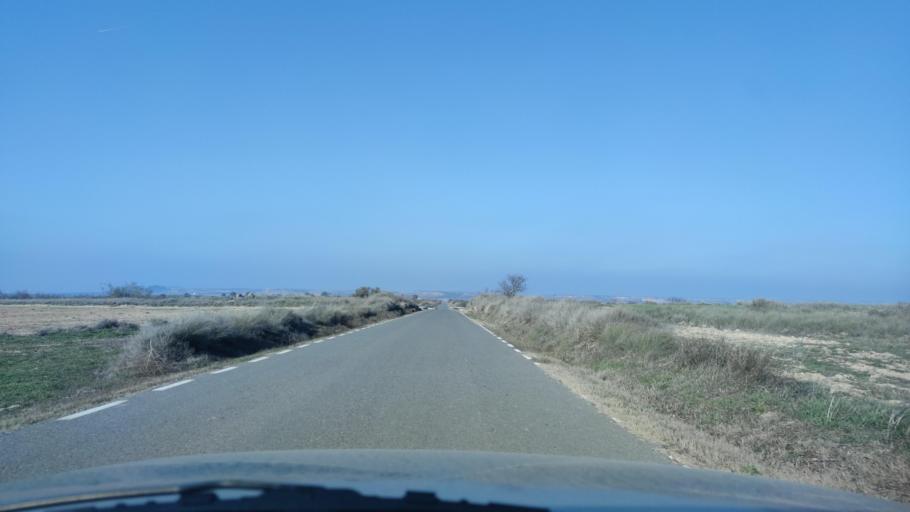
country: ES
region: Catalonia
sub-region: Provincia de Lleida
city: Sunyer
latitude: 41.4870
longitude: 0.5603
